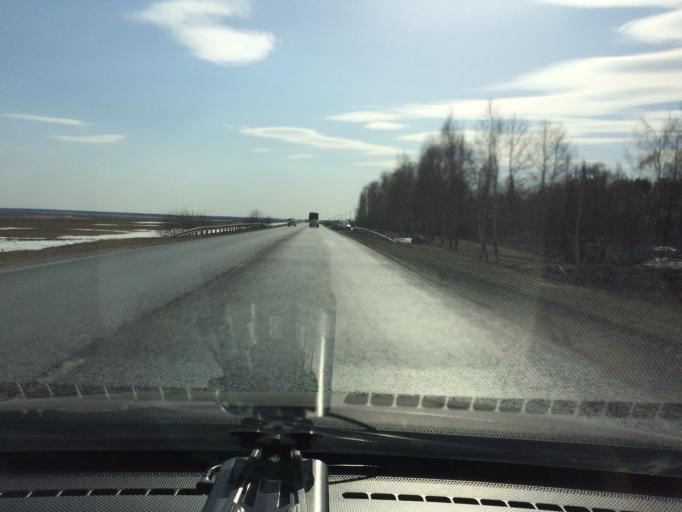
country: RU
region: Mariy-El
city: Yoshkar-Ola
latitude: 56.7036
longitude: 48.0731
